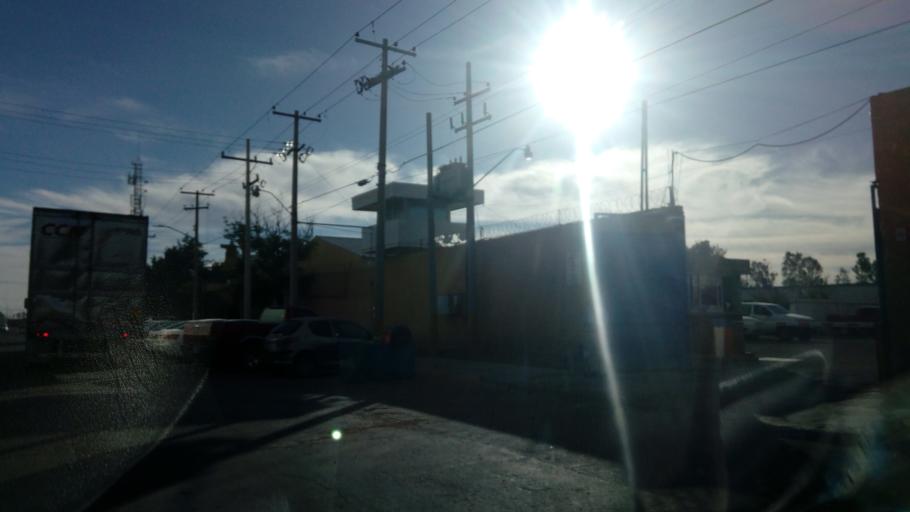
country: MX
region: Durango
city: Victoria de Durango
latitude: 24.0688
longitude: -104.6067
